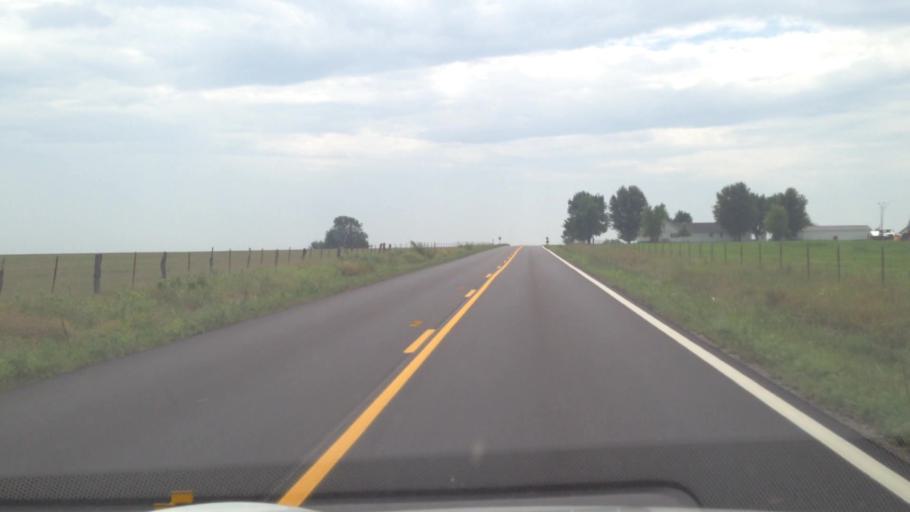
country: US
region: Kansas
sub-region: Crawford County
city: Girard
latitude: 37.5481
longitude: -94.9605
